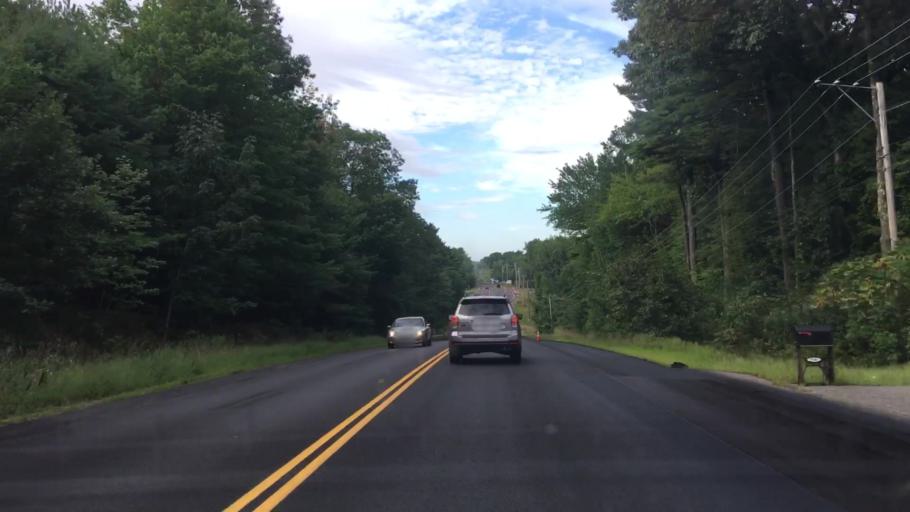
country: US
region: Maine
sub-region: York County
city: South Sanford
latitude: 43.4196
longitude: -70.7371
